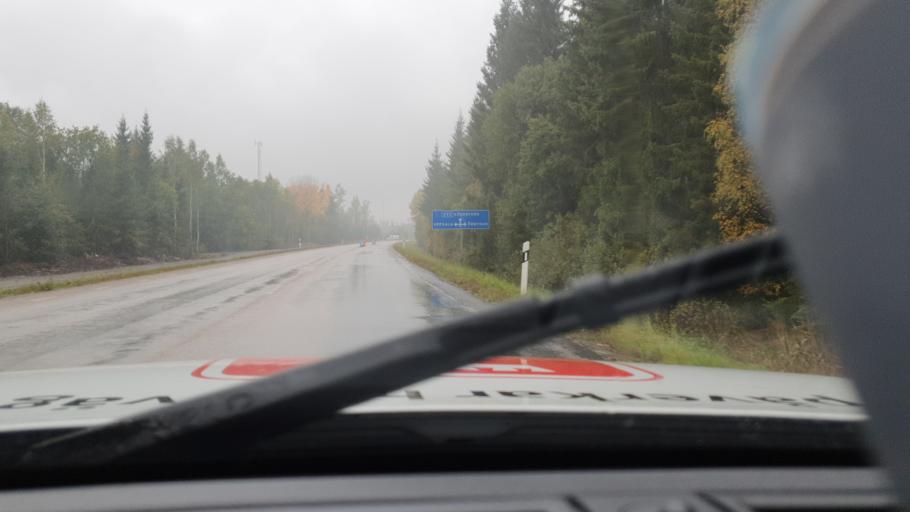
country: SE
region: Uppsala
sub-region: Tierps Kommun
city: Orbyhus
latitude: 60.2157
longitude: 17.7087
